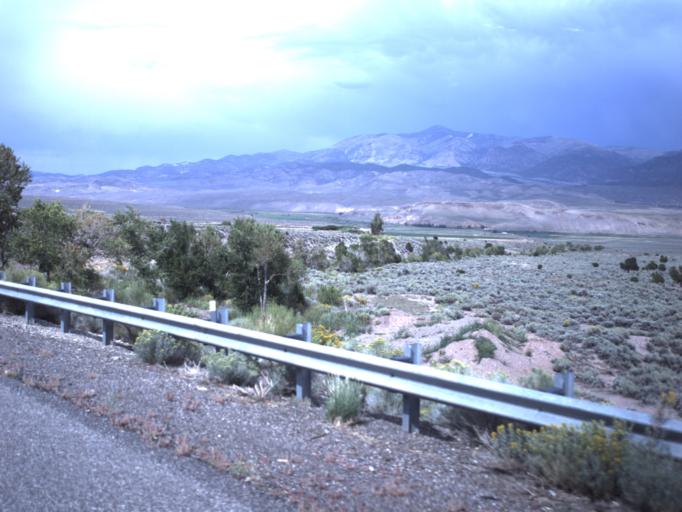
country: US
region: Utah
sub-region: Piute County
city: Junction
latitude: 38.3444
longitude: -112.2185
